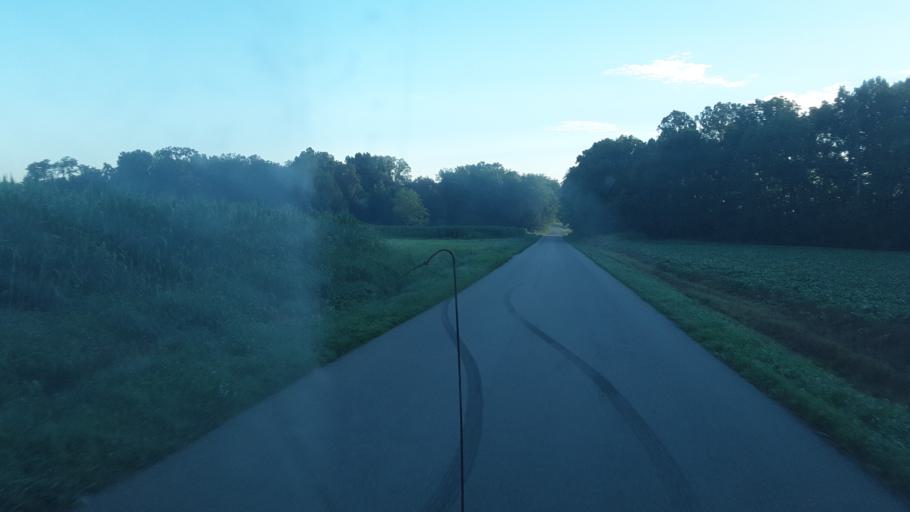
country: US
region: Kentucky
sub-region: Todd County
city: Guthrie
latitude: 36.7281
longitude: -87.1683
